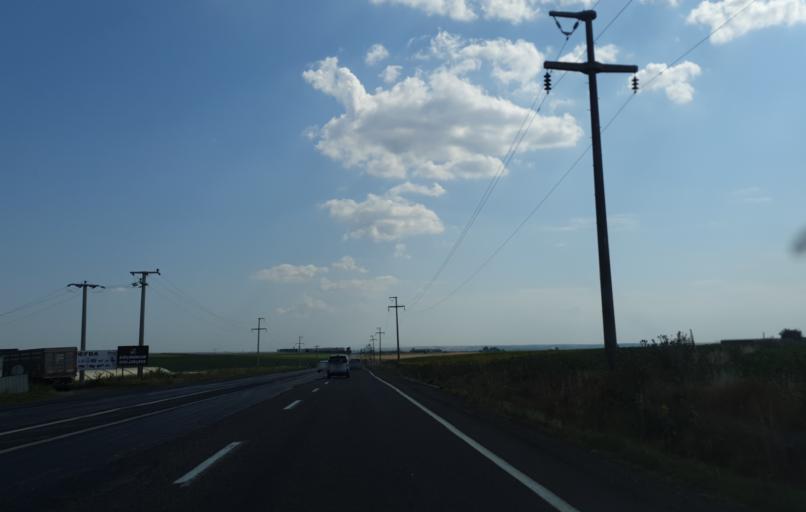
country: TR
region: Kirklareli
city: Buyukkaristiran
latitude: 41.2674
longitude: 27.5503
